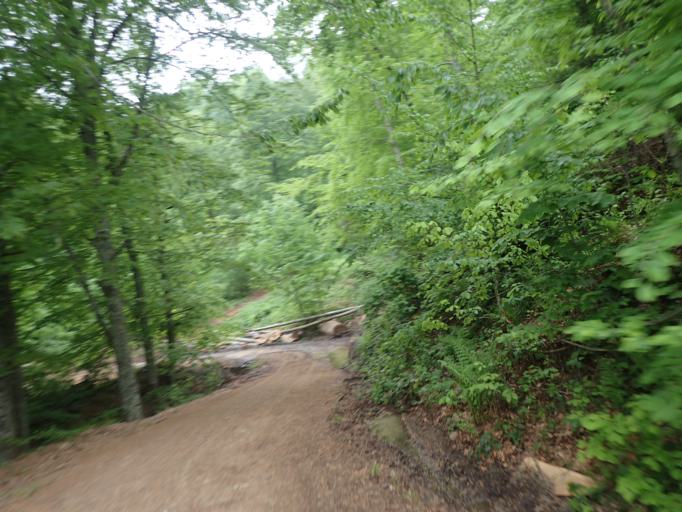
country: TR
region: Ordu
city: Akkus
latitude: 40.8700
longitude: 37.0851
